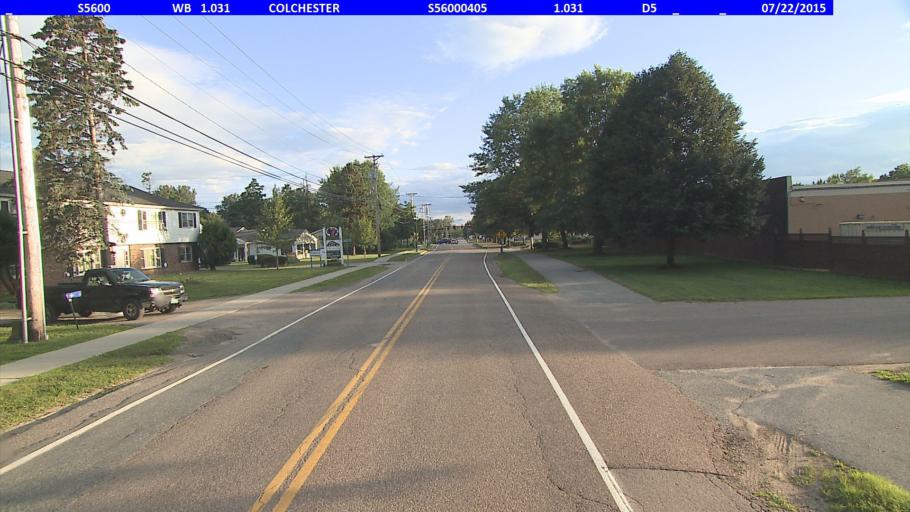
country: US
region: Vermont
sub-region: Chittenden County
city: Burlington
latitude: 44.5381
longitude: -73.2466
